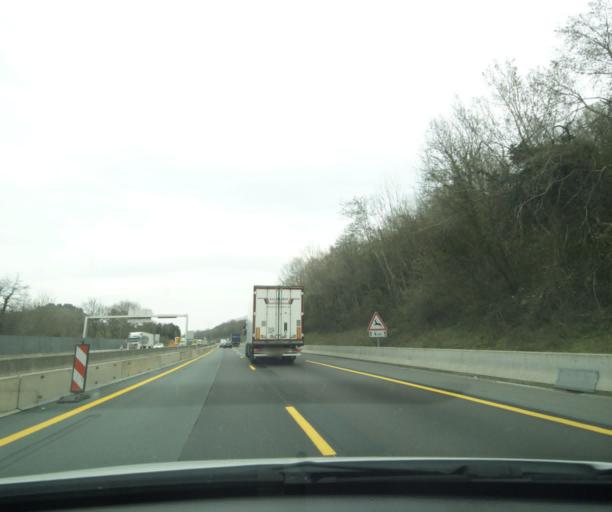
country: FR
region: Aquitaine
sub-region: Departement des Pyrenees-Atlantiques
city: Hendaye
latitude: 43.3412
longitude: -1.7443
